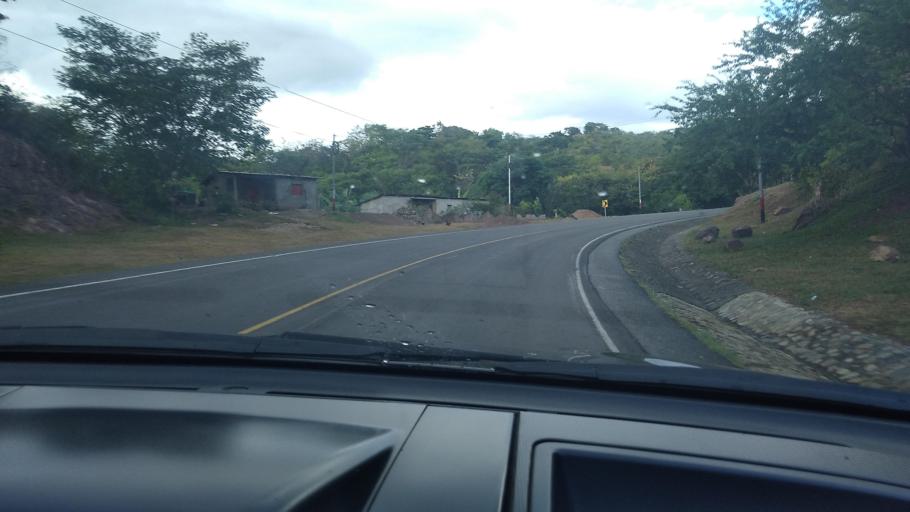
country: NI
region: Madriz
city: Yalaguina
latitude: 13.4947
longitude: -86.5020
